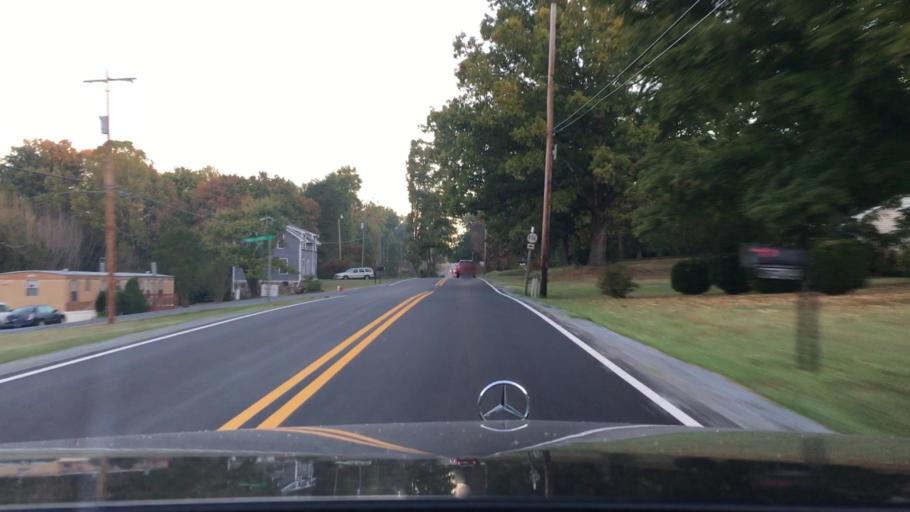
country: US
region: Virginia
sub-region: Campbell County
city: Timberlake
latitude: 37.3028
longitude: -79.2330
